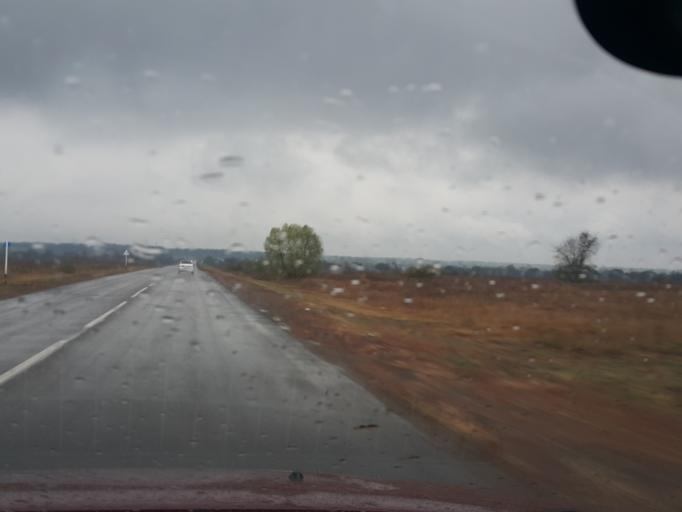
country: RU
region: Tambov
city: Kotovsk
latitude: 52.5327
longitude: 41.4953
